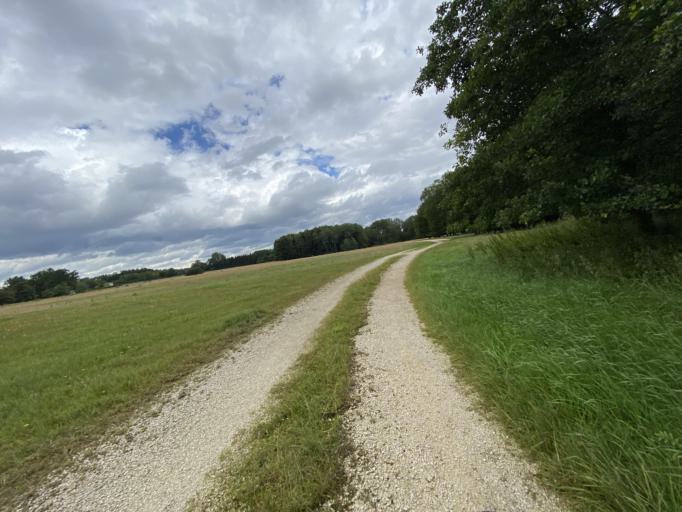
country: DE
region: Baden-Wuerttemberg
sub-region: Tuebingen Region
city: Sigmaringendorf
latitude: 48.0886
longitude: 9.2569
